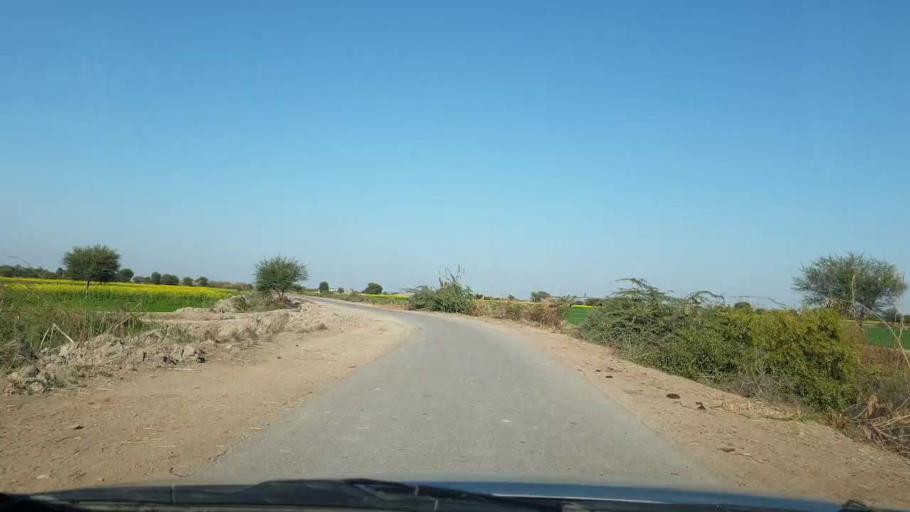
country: PK
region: Sindh
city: Jhol
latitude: 25.8280
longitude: 68.9494
